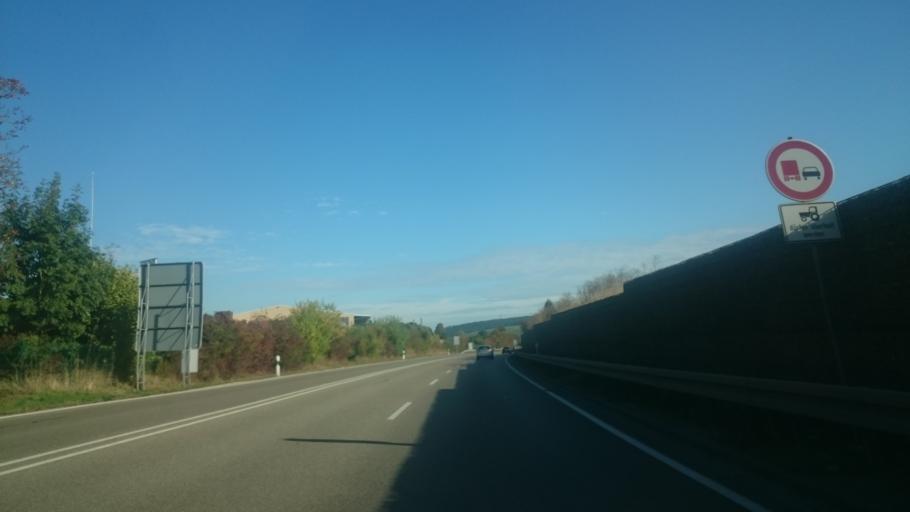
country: DE
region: Bavaria
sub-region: Regierungsbezirk Mittelfranken
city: Ellingen
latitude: 49.0664
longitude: 10.9609
